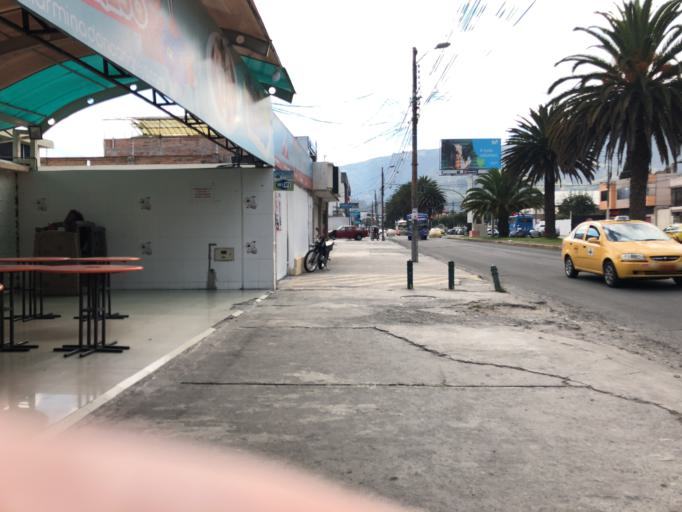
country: EC
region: Imbabura
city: Ibarra
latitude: 0.3481
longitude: -78.1278
